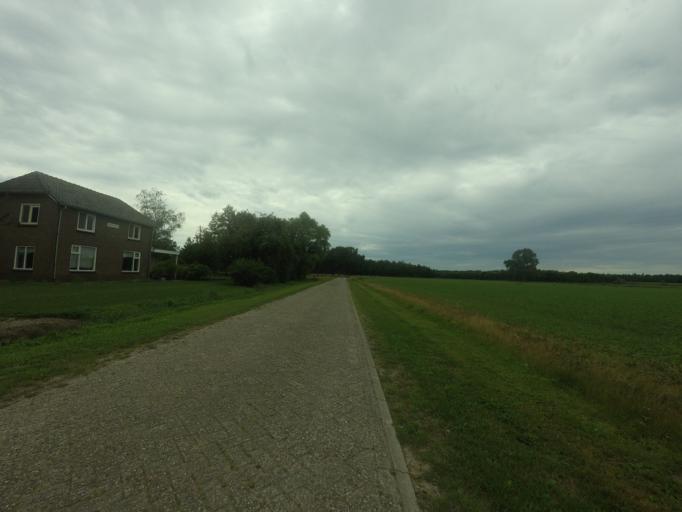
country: NL
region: Overijssel
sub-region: Gemeente Raalte
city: Raalte
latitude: 52.3510
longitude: 6.3260
